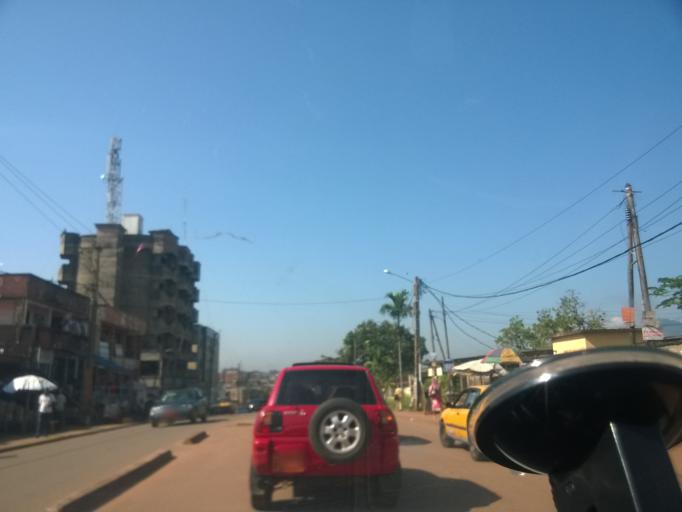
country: CM
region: Centre
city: Yaounde
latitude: 3.8405
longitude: 11.4882
